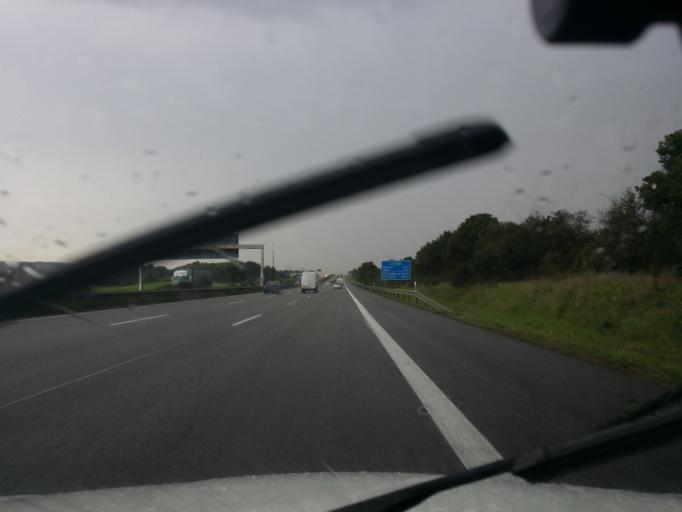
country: DE
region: Thuringia
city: Wandersleben
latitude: 50.8779
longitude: 10.8190
